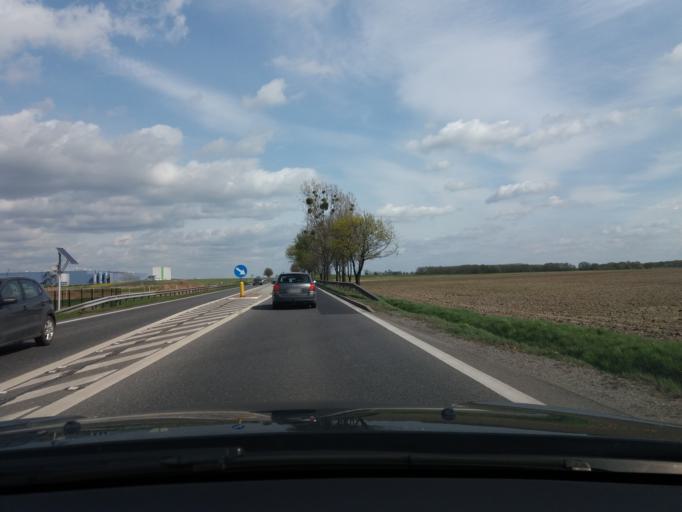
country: PL
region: Lower Silesian Voivodeship
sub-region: Powiat sredzki
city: Szczepanow
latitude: 51.1648
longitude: 16.6431
